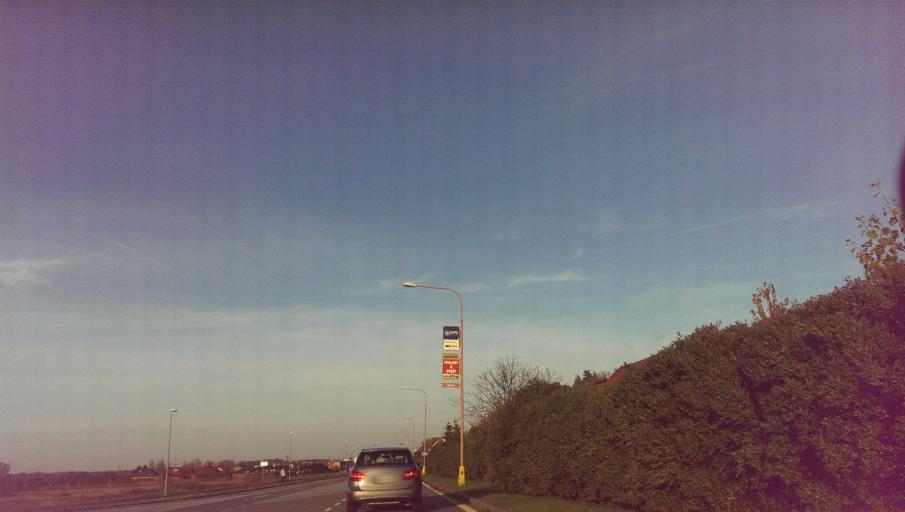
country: CZ
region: Zlin
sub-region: Okres Uherske Hradiste
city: Uherske Hradiste
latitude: 49.0783
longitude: 17.4855
